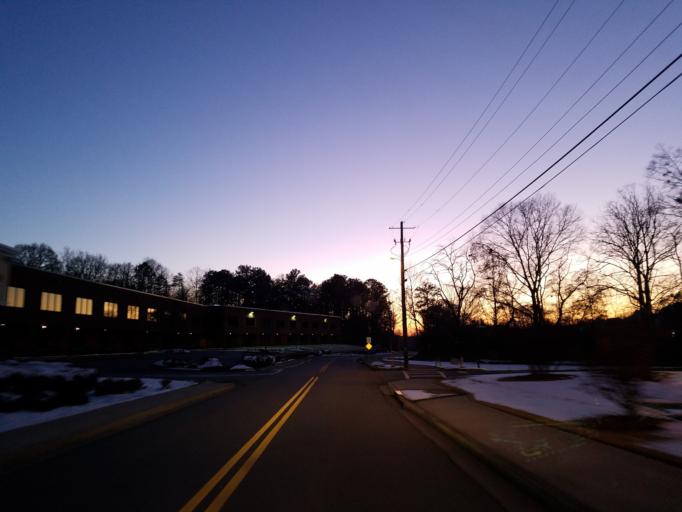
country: US
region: Georgia
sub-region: Cherokee County
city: Ball Ground
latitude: 34.3348
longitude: -84.3789
